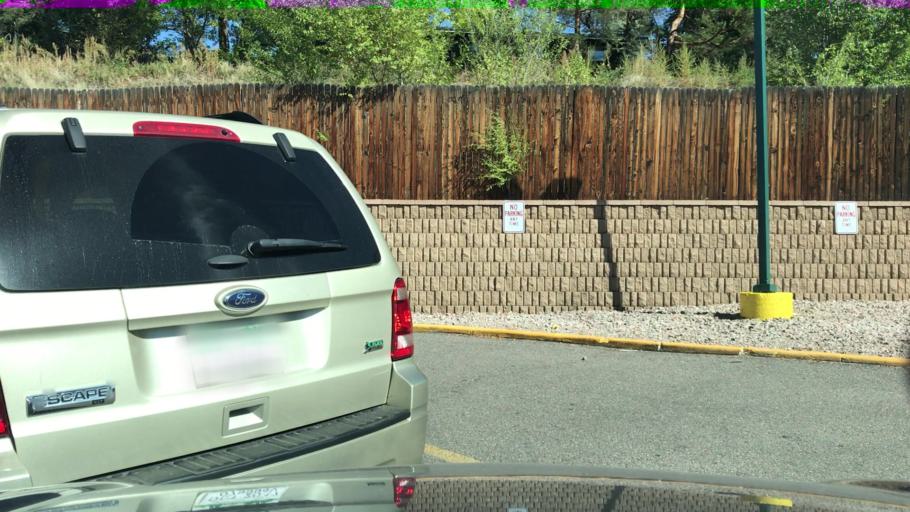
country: US
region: Colorado
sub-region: Arapahoe County
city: Glendale
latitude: 39.7072
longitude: -104.9204
